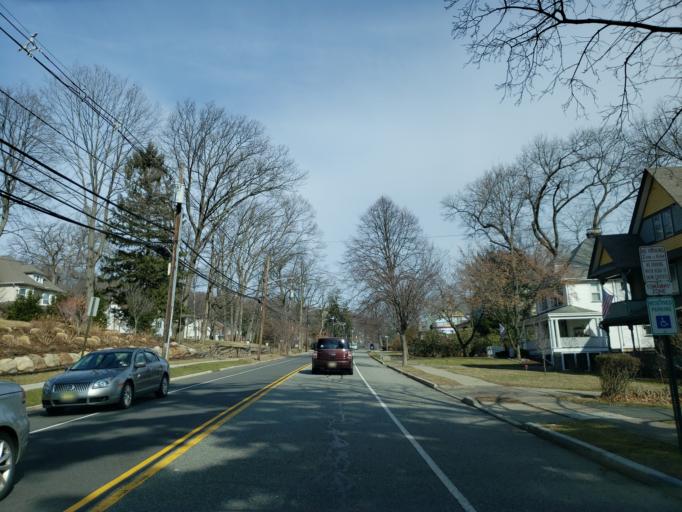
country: US
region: New Jersey
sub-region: Essex County
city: Verona
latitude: 40.8372
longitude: -74.2501
